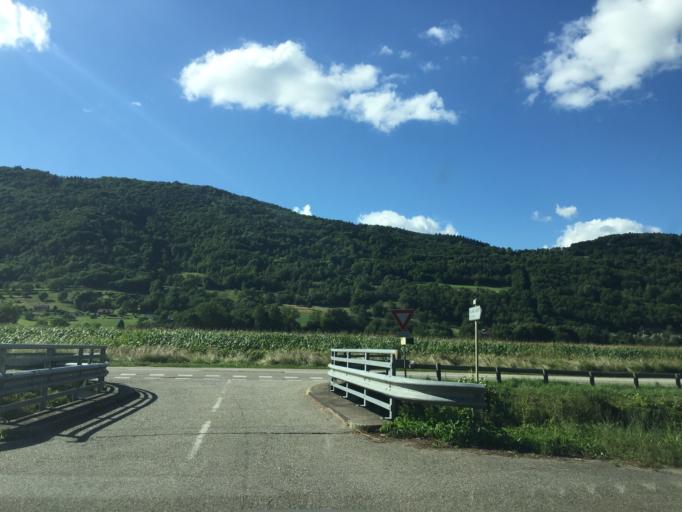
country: FR
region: Rhone-Alpes
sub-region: Departement de la Savoie
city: Coise-Saint-Jean-Pied-Gauthier
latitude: 45.4962
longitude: 6.1592
